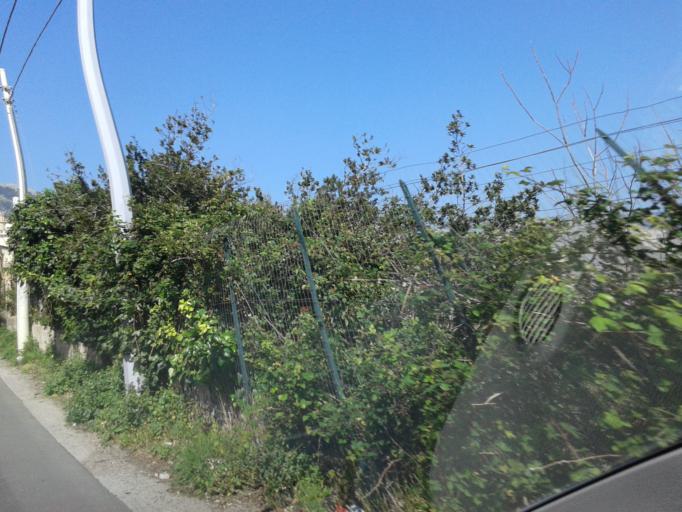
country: IT
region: Sicily
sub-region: Palermo
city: Piano dei Geli
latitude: 38.1094
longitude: 13.3020
